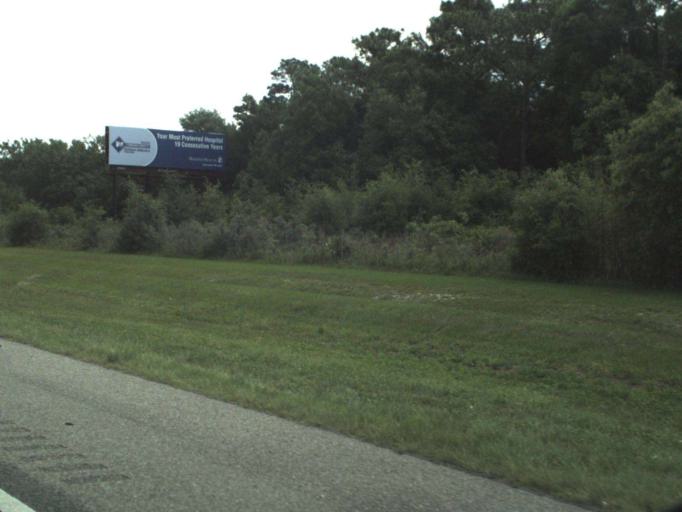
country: US
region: Florida
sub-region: Volusia County
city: Lake Helen
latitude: 28.9820
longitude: -81.2490
